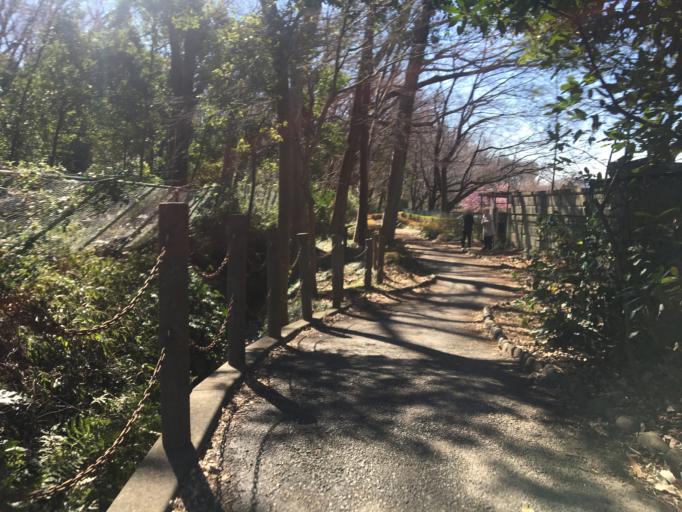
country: JP
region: Saitama
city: Asaka
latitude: 35.7930
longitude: 139.5565
